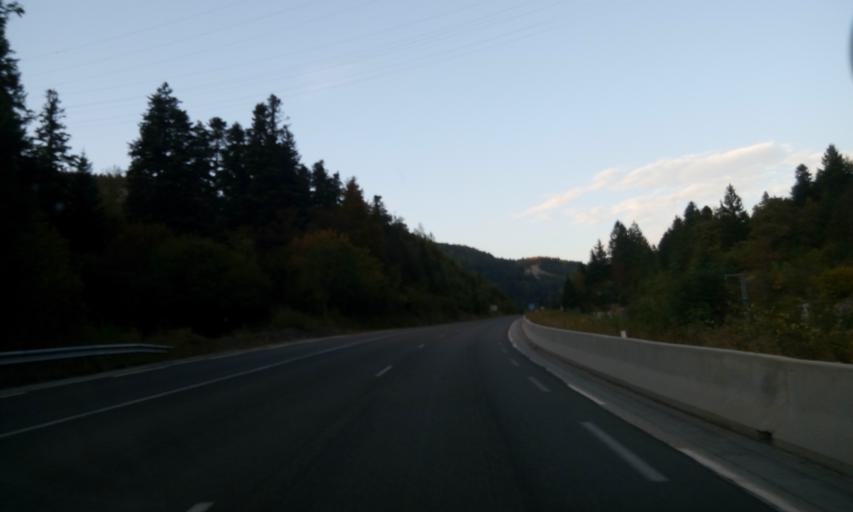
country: FR
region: Rhone-Alpes
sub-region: Departement de l'Ain
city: Nantua
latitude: 46.1525
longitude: 5.6485
